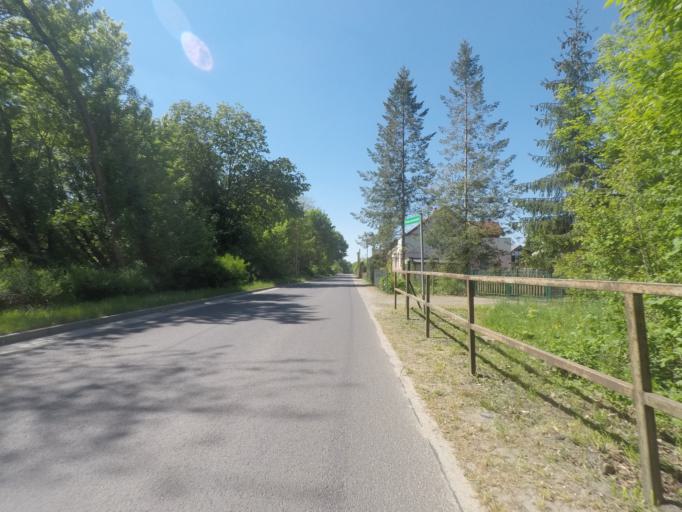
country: DE
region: Brandenburg
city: Melchow
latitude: 52.8502
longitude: 13.7099
